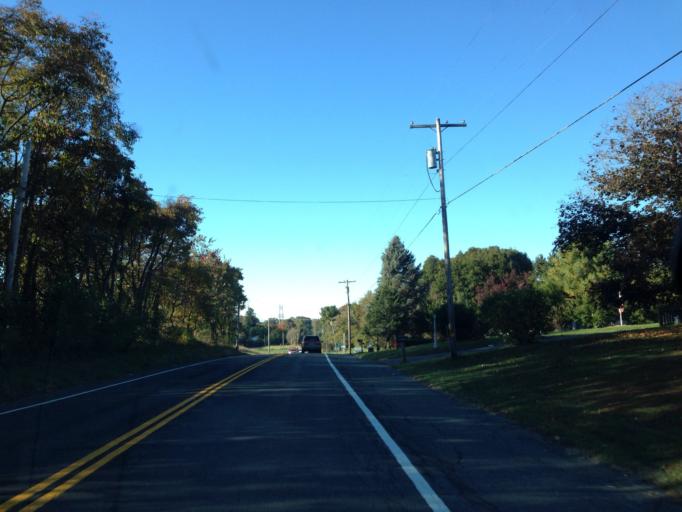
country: US
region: Maryland
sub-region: Montgomery County
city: Damascus
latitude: 39.3318
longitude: -77.1891
